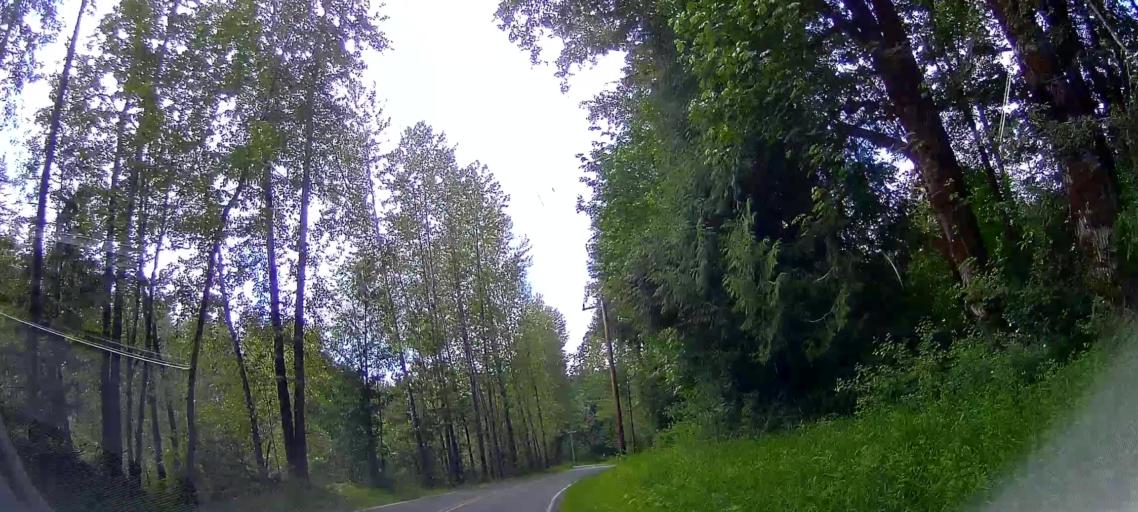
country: US
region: Washington
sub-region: Skagit County
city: Sedro-Woolley
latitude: 48.6757
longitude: -122.1570
